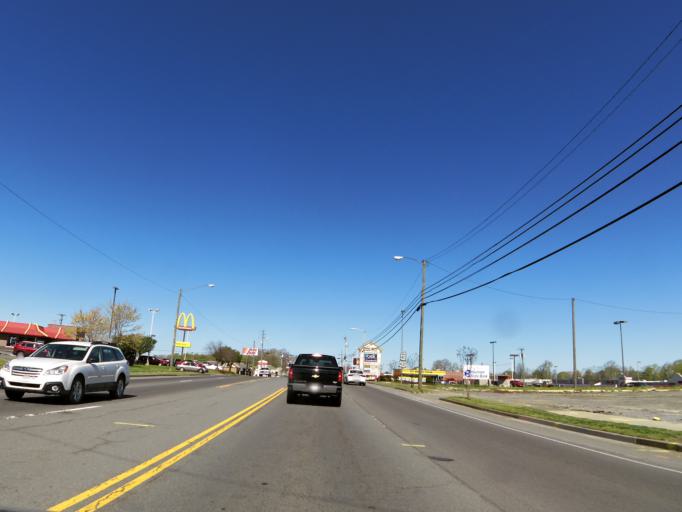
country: US
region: Tennessee
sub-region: Robertson County
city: Springfield
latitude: 36.4932
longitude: -86.8759
